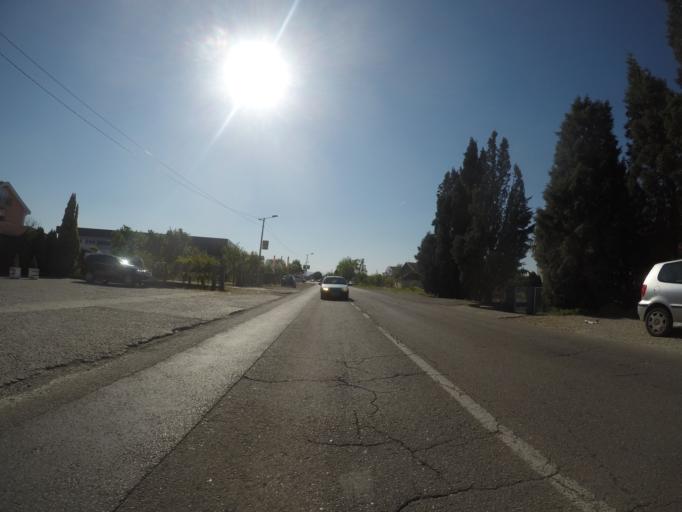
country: ME
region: Podgorica
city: Podgorica
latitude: 42.4411
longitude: 19.2174
